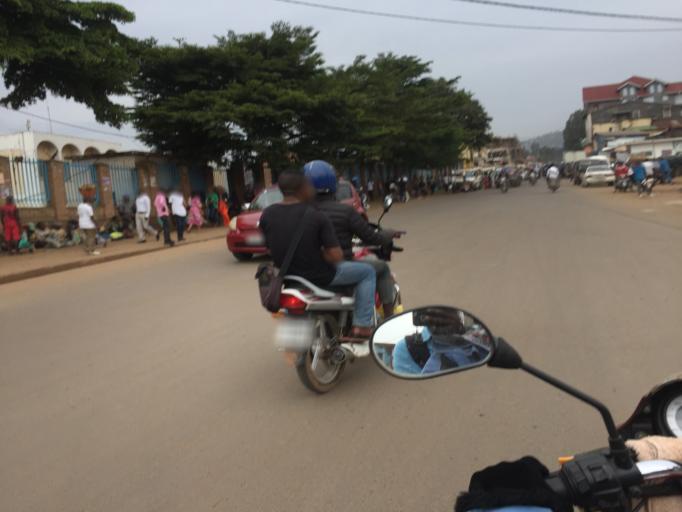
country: CD
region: South Kivu
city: Bukavu
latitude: -2.5061
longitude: 28.8619
